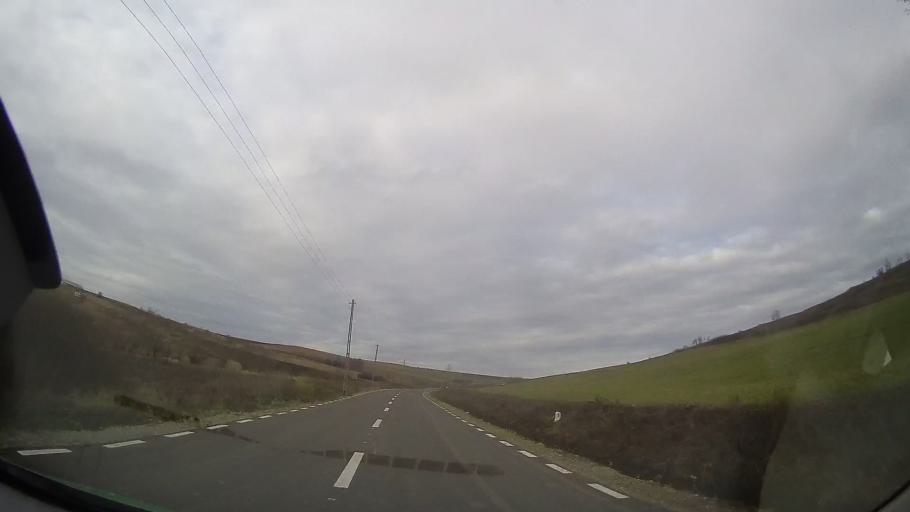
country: RO
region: Mures
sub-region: Comuna Cozma
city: Cozma
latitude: 46.8171
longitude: 24.4915
